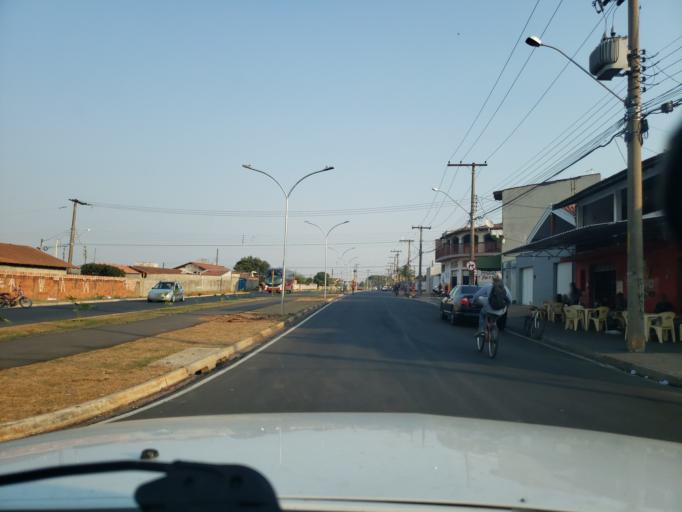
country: BR
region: Sao Paulo
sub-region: Moji-Guacu
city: Mogi-Gaucu
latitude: -22.3281
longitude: -46.9503
